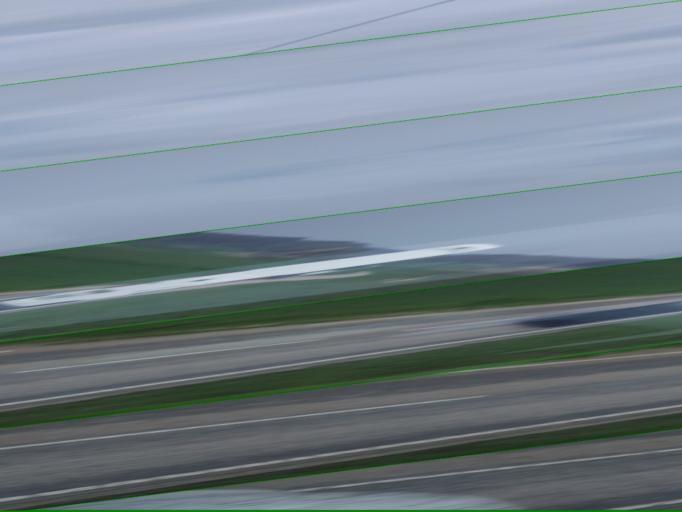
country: FR
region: Ile-de-France
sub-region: Departement des Yvelines
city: Houdan
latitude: 48.8093
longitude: 1.5988
